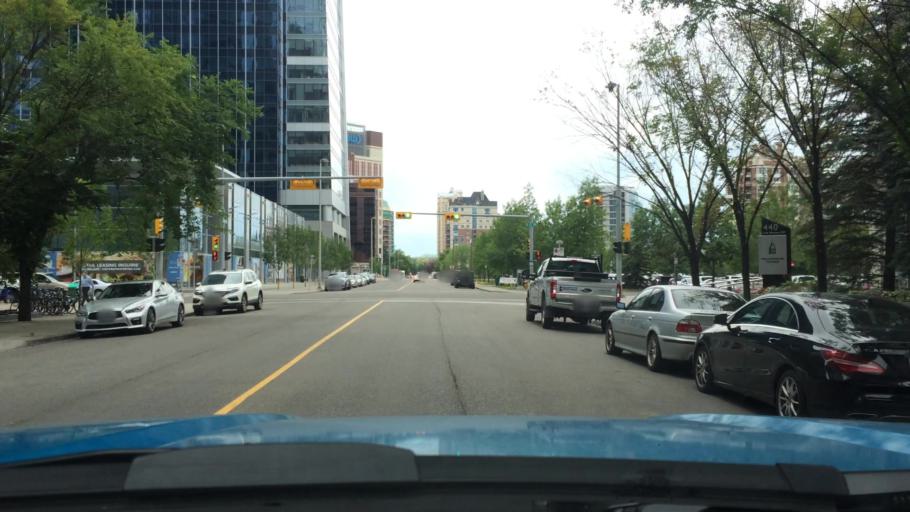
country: CA
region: Alberta
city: Calgary
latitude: 51.0515
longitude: -114.0708
